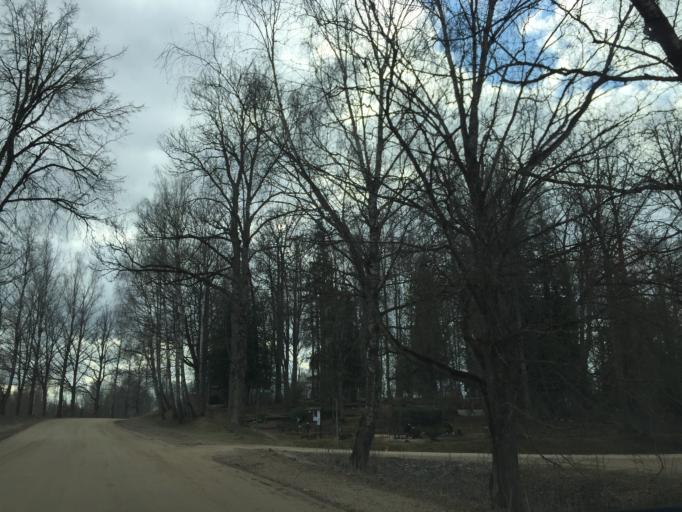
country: LV
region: Vecumnieki
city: Vecumnieki
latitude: 56.5059
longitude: 24.7189
